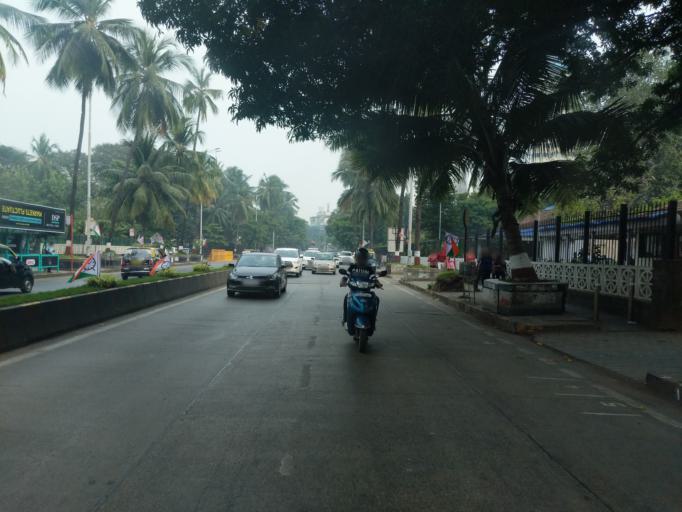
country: IN
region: Maharashtra
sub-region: Raigarh
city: Uran
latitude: 18.9279
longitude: 72.8247
